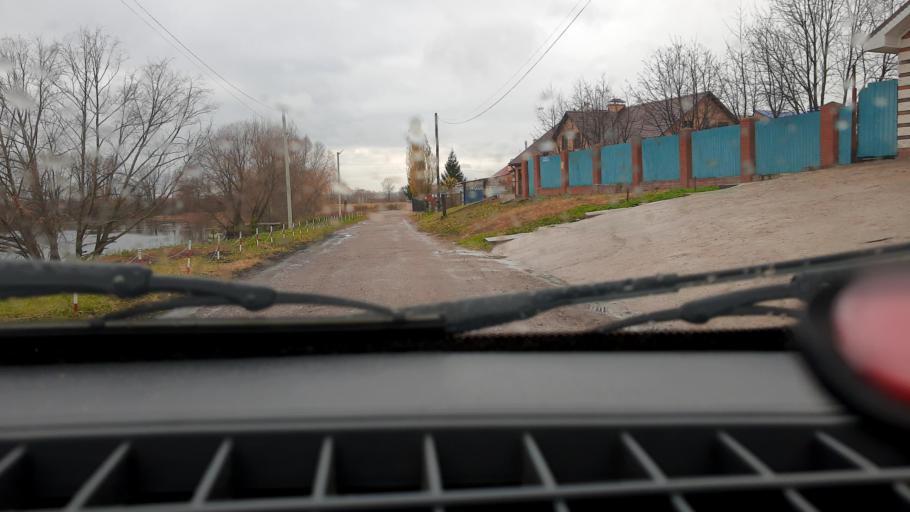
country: RU
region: Bashkortostan
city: Ufa
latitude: 54.8195
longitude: 55.9903
